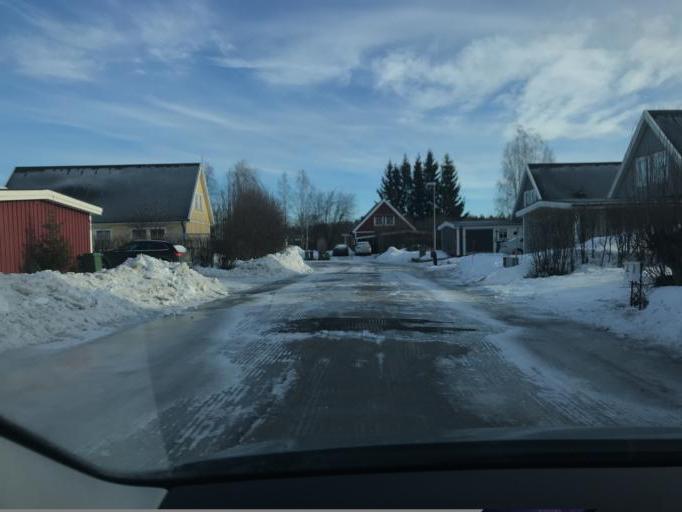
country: SE
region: Norrbotten
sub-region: Lulea Kommun
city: Sodra Sunderbyn
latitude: 65.6496
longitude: 21.9609
